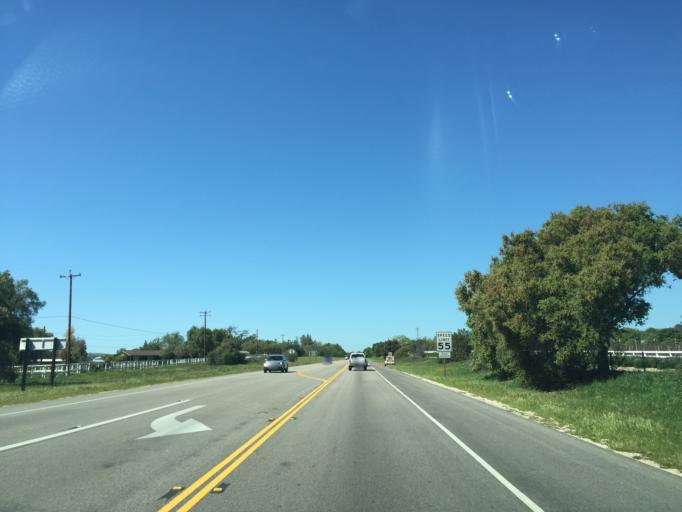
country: US
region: California
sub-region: Santa Barbara County
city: Los Olivos
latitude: 34.6516
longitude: -120.0962
